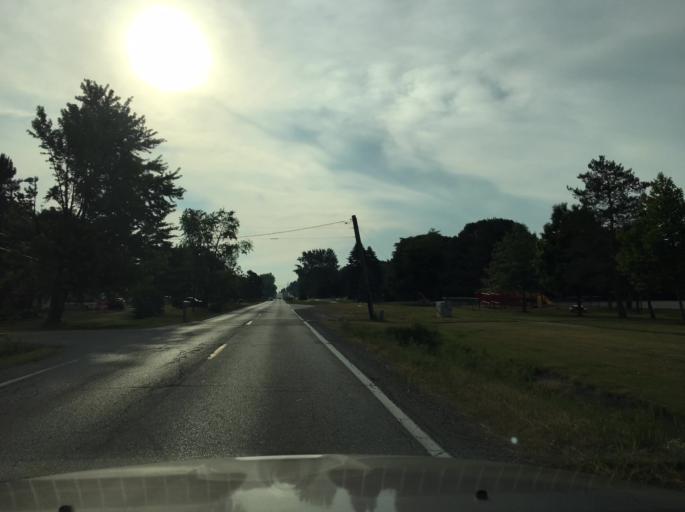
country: US
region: Michigan
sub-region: Macomb County
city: Utica
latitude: 42.6407
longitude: -83.0235
